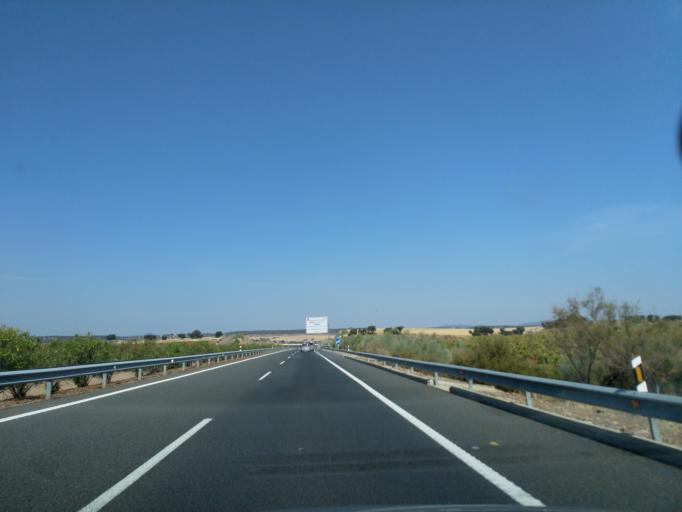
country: ES
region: Extremadura
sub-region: Provincia de Badajoz
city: Aljucen
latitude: 39.0325
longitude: -6.3358
